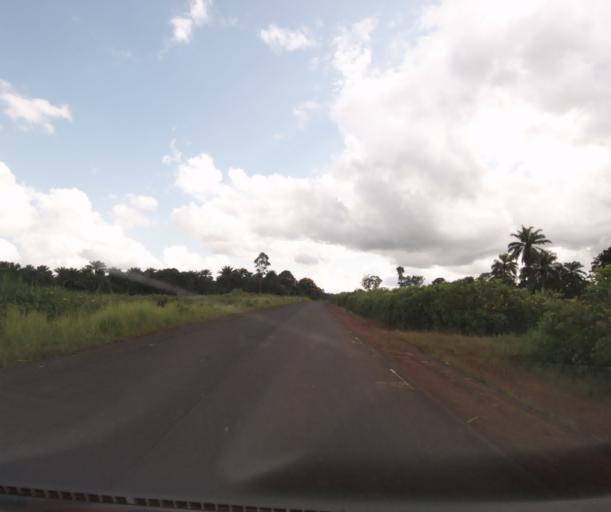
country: CM
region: West
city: Foumban
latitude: 5.6925
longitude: 10.8101
